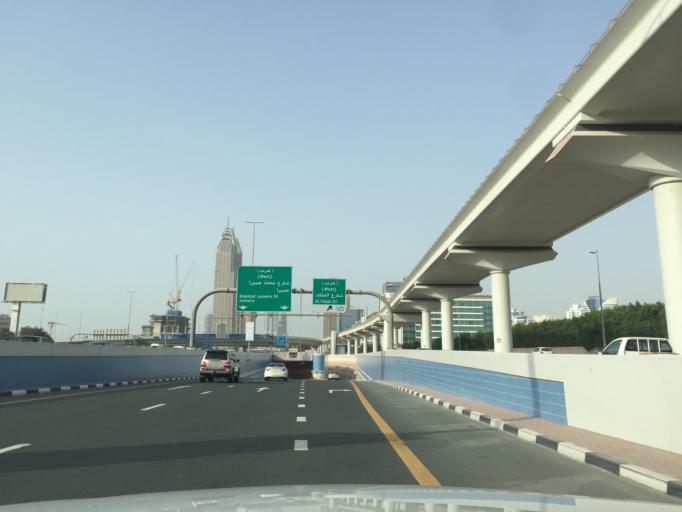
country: AE
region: Dubai
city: Dubai
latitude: 25.0922
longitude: 55.1619
